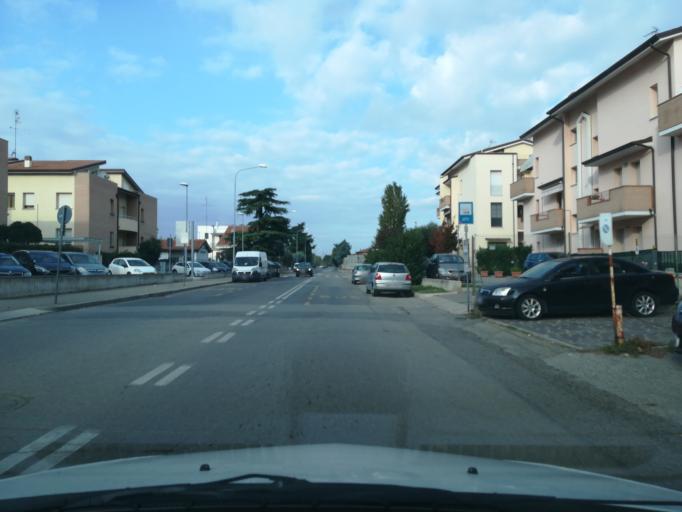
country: IT
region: Emilia-Romagna
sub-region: Provincia di Bologna
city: Imola
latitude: 44.3644
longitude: 11.7150
